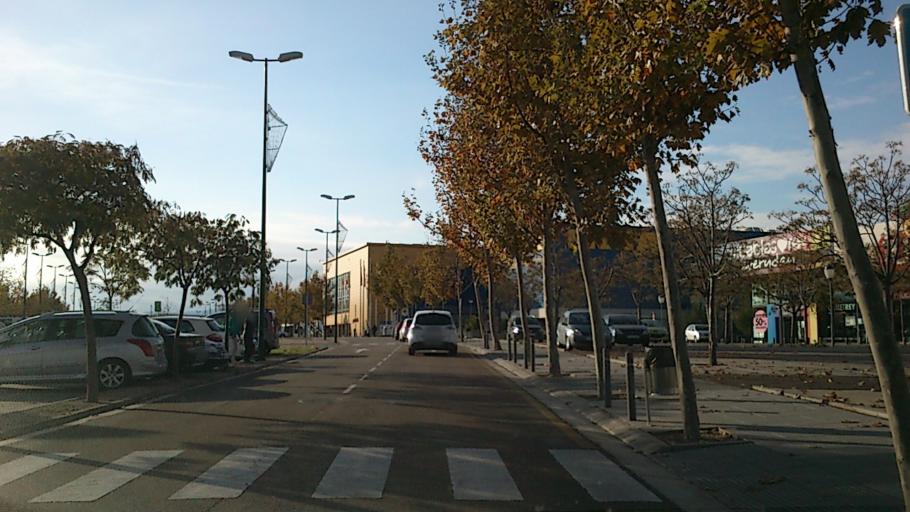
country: ES
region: Aragon
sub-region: Provincia de Zaragoza
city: Delicias
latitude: 41.6093
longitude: -0.8905
